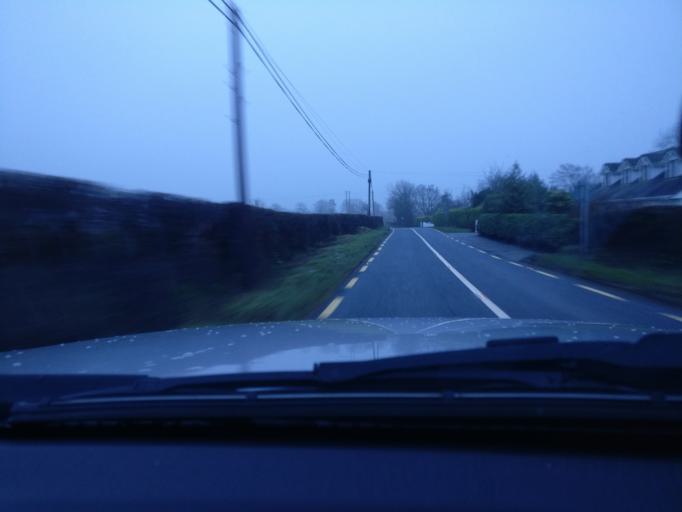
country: IE
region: Leinster
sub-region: An Mhi
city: Ballivor
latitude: 53.6114
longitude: -7.0465
